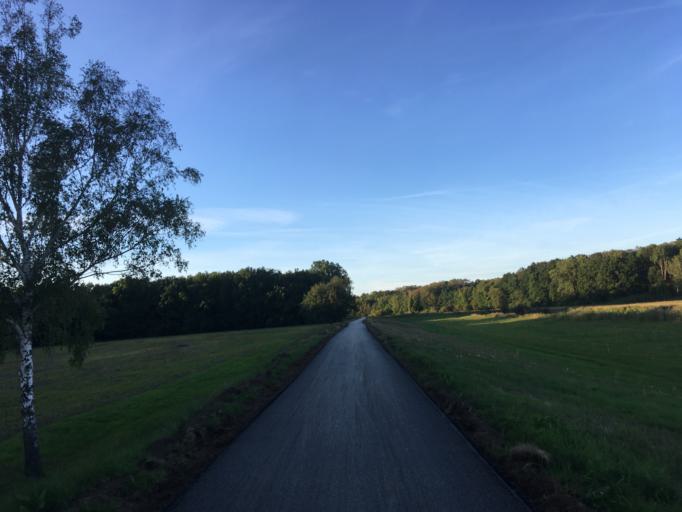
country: DE
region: Brandenburg
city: Forst
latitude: 51.7188
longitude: 14.6784
